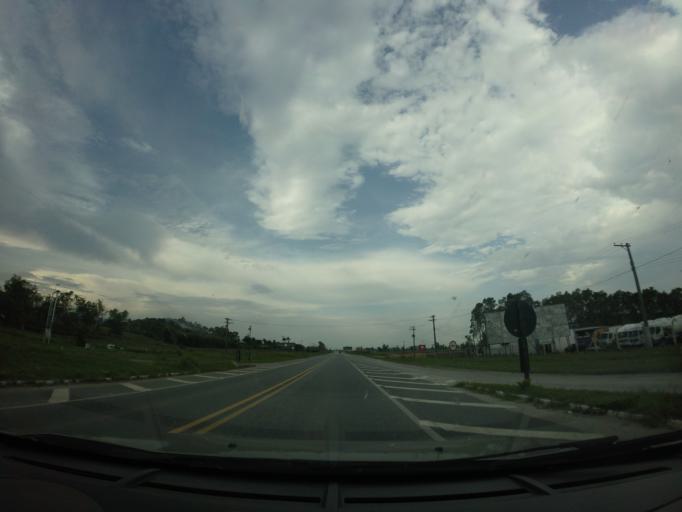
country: BR
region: Sao Paulo
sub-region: Tremembe
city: Tremembe
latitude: -22.9448
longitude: -45.6060
